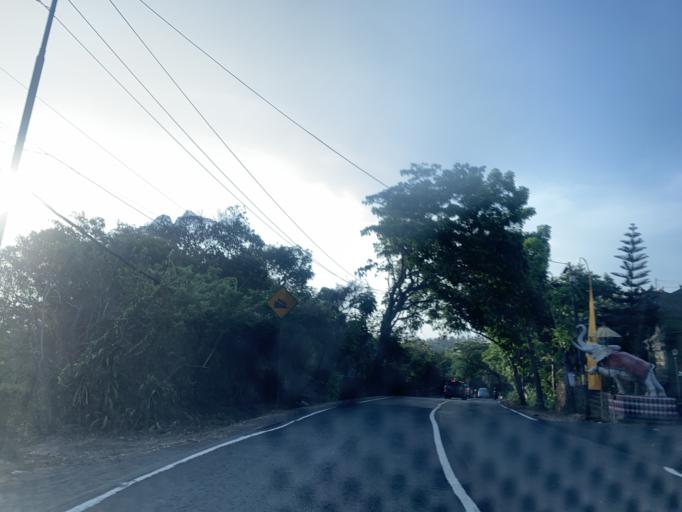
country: ID
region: Bali
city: Banjar Delodrurung
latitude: -8.5005
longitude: 114.9698
